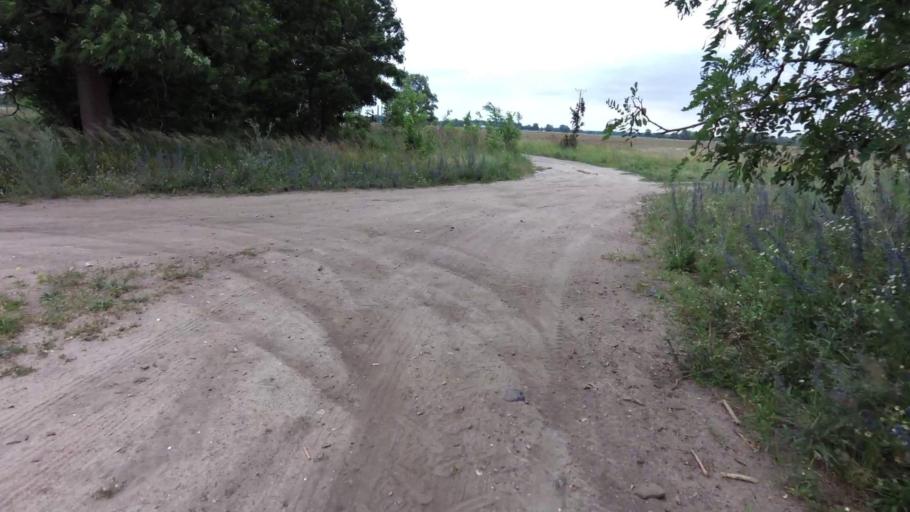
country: PL
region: Lubusz
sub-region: Powiat gorzowski
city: Kostrzyn nad Odra
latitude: 52.6139
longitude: 14.6051
